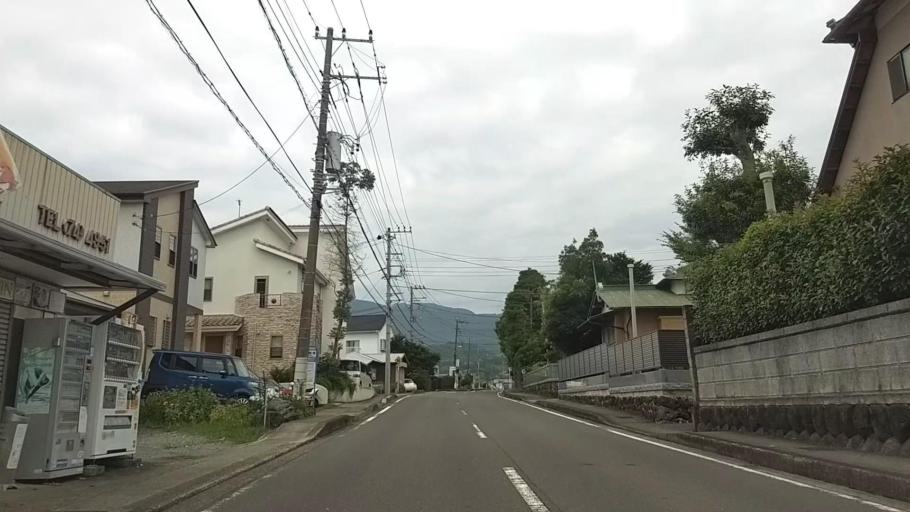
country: JP
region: Kanagawa
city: Odawara
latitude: 35.3275
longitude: 139.0885
